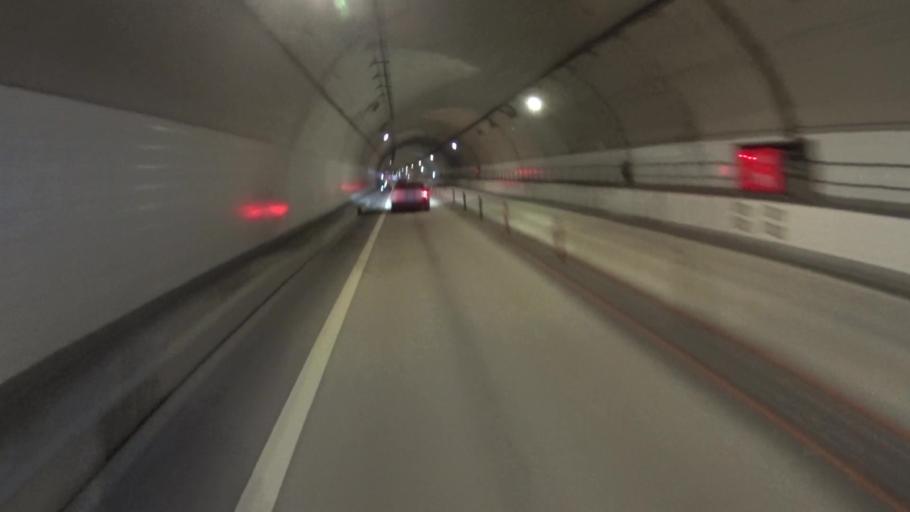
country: JP
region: Kyoto
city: Miyazu
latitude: 35.5319
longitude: 135.1687
